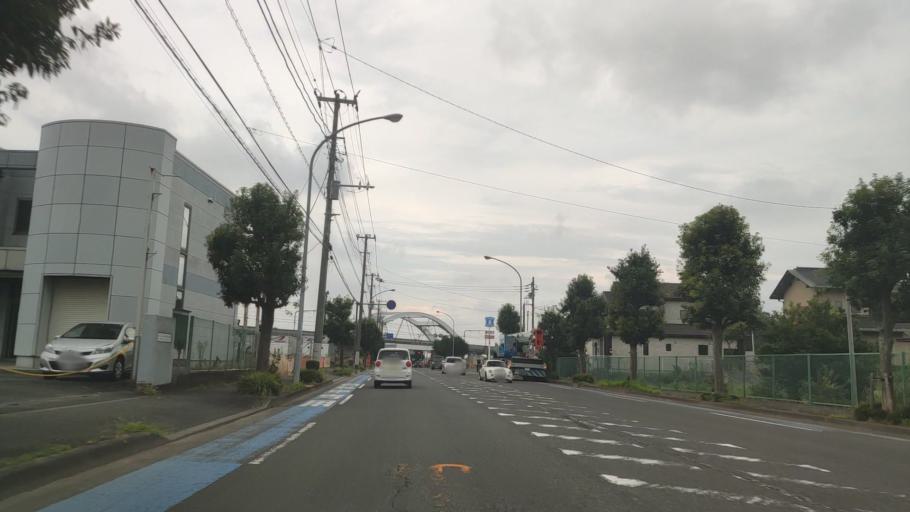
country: JP
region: Kanagawa
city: Fujisawa
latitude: 35.4096
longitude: 139.4841
